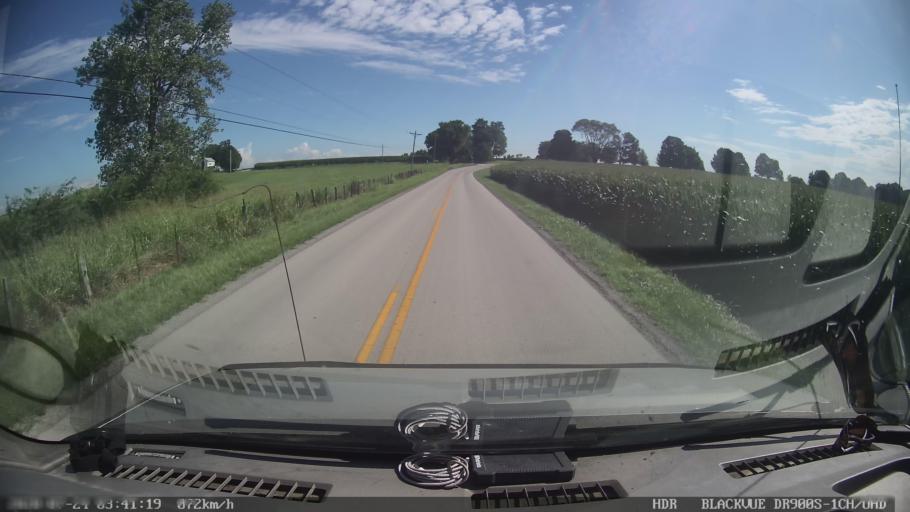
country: US
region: Kentucky
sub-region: Todd County
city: Guthrie
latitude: 36.7318
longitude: -87.2582
